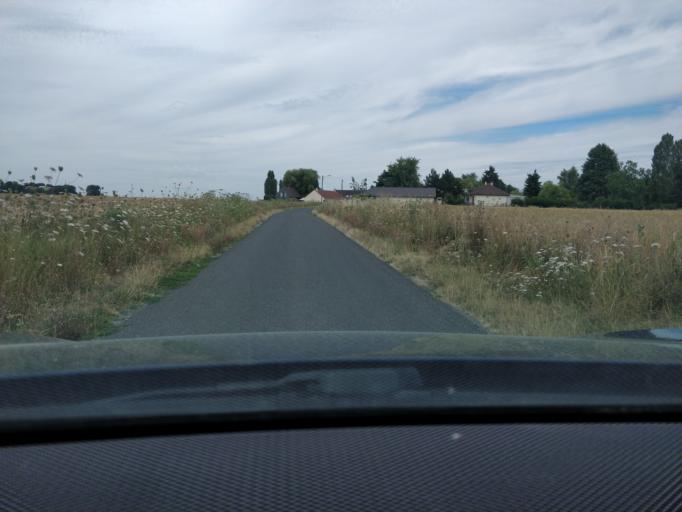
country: FR
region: Ile-de-France
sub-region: Departement de l'Essonne
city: Briis-sous-Forges
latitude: 48.6373
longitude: 2.1295
